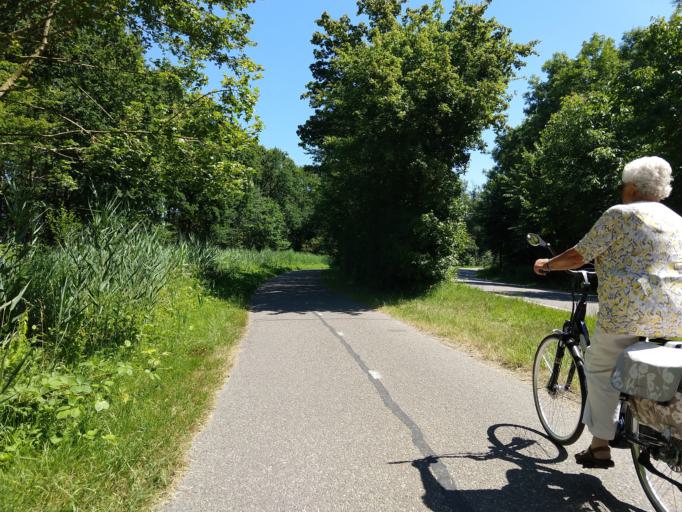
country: NL
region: Zeeland
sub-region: Gemeente Veere
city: Veere
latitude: 51.5541
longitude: 3.6567
